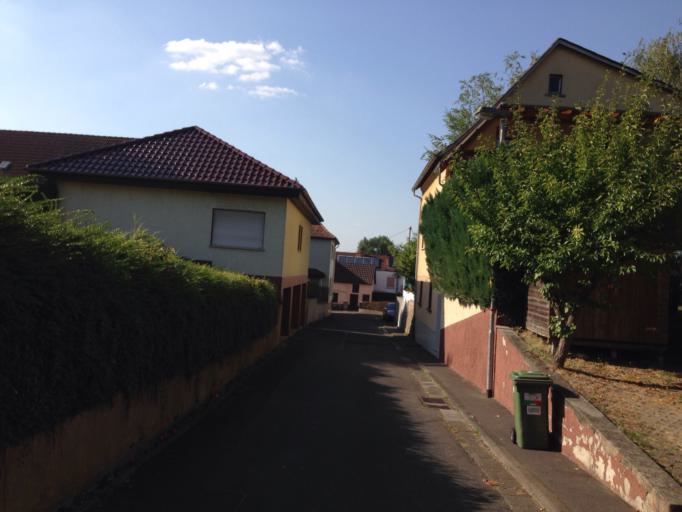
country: DE
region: Hesse
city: Staufenberg
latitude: 50.6515
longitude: 8.7411
